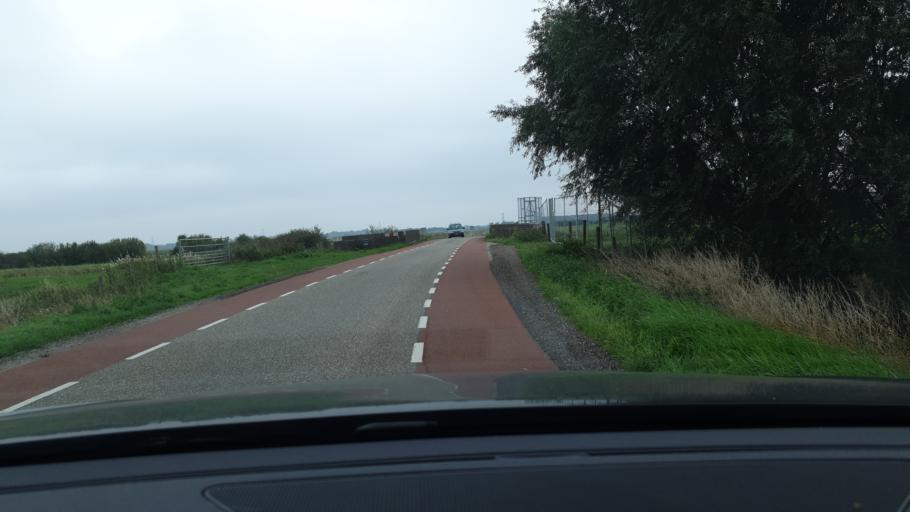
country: NL
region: North Brabant
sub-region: Gemeente Maasdonk
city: Geffen
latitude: 51.7714
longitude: 5.4591
